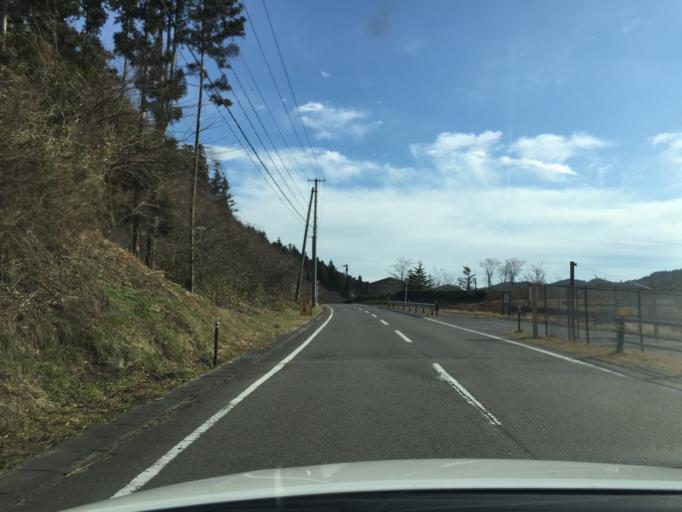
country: JP
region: Fukushima
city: Funehikimachi-funehiki
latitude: 37.2811
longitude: 140.5850
